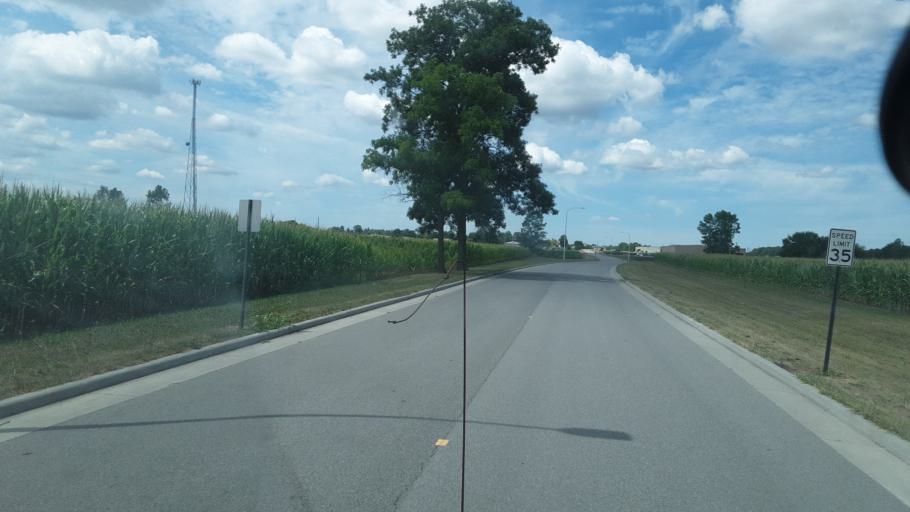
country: US
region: Ohio
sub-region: Defiance County
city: Hicksville
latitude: 41.3069
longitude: -84.7550
